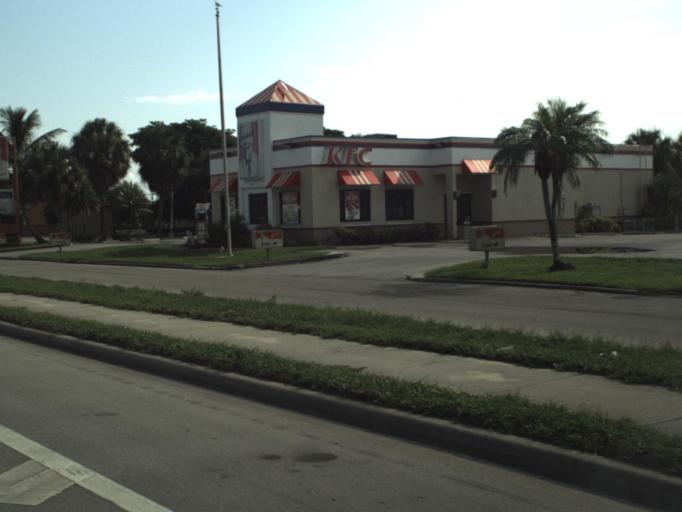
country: US
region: Florida
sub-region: Palm Beach County
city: Belle Glade
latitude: 26.6732
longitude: -80.6704
